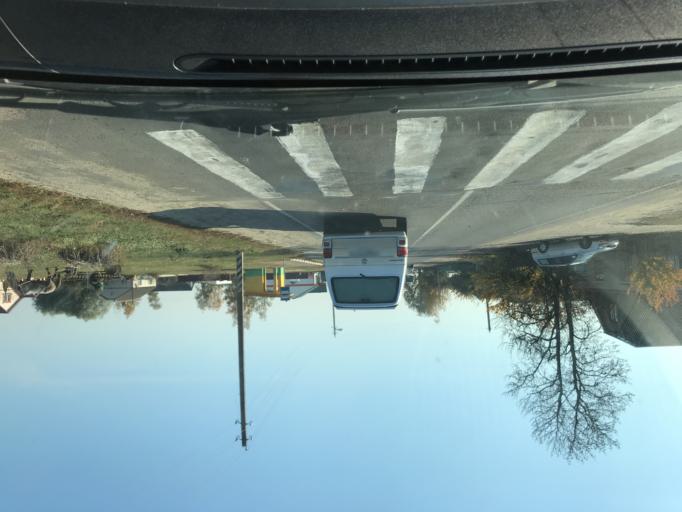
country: BY
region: Brest
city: Davyd-Haradok
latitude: 52.0601
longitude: 27.2832
